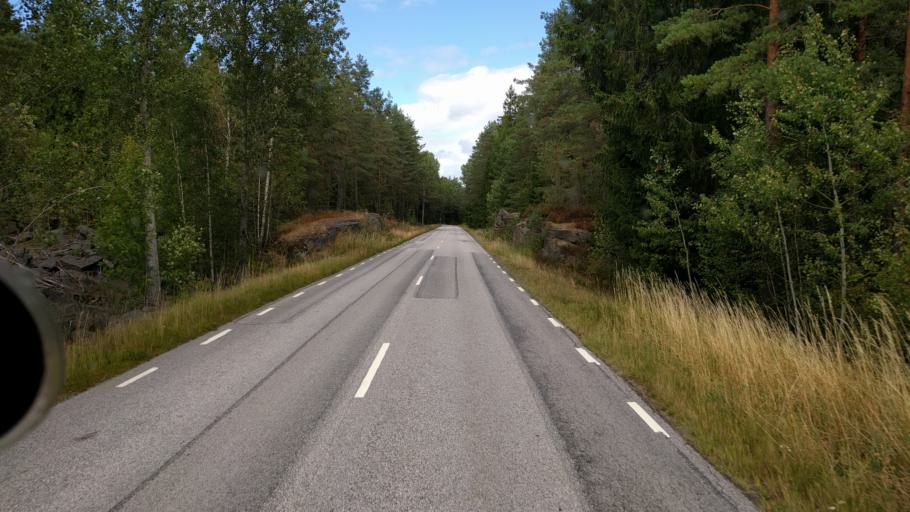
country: SE
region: Kalmar
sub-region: Vasterviks Kommun
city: Ankarsrum
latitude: 57.7466
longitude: 16.1126
